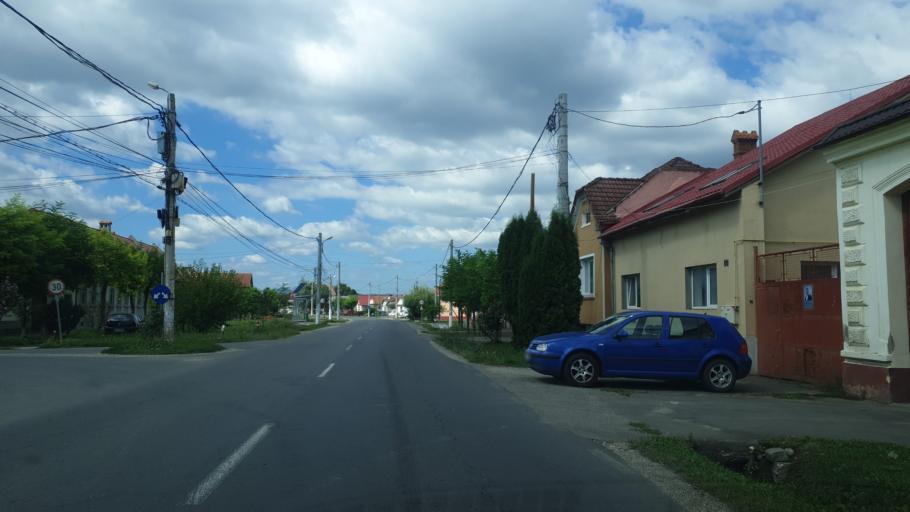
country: RO
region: Brasov
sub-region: Comuna Sanpetru
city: Sanpetru
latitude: 45.7150
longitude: 25.6307
